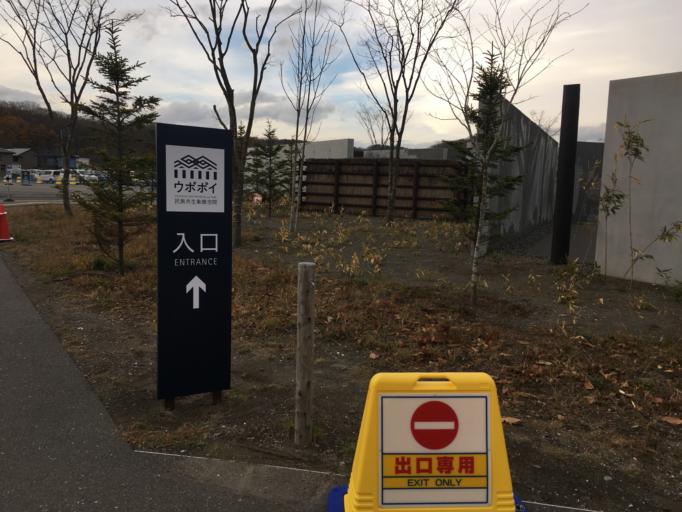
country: JP
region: Hokkaido
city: Shiraoi
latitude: 42.5583
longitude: 141.3639
